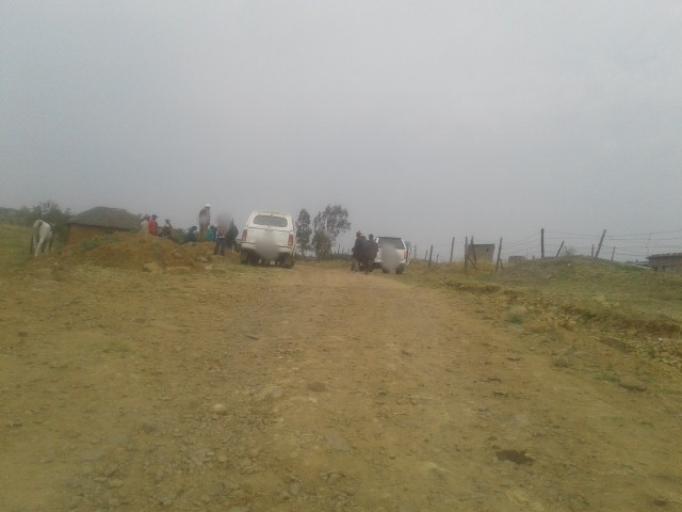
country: LS
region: Berea
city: Teyateyaneng
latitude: -29.0867
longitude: 27.9056
